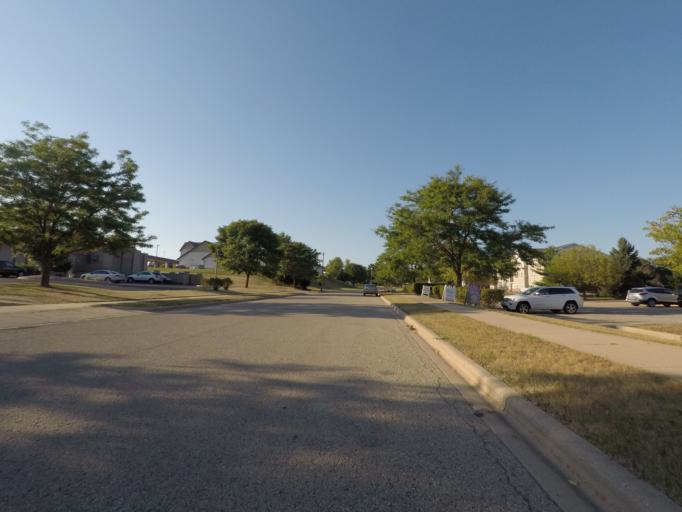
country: US
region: Wisconsin
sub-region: Dane County
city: Verona
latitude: 43.0024
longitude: -89.5322
